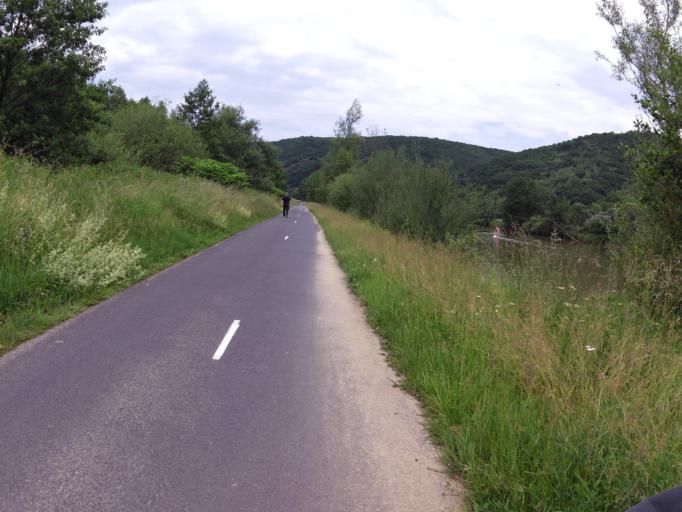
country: FR
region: Champagne-Ardenne
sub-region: Departement des Ardennes
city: Aiglemont
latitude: 49.7939
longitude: 4.7578
